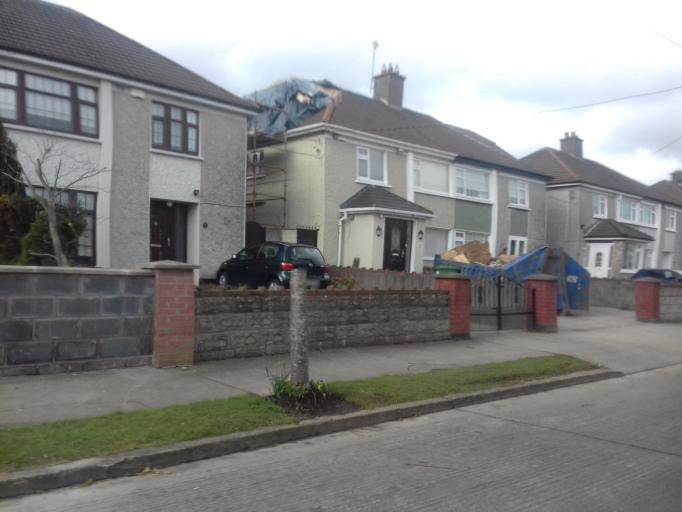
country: IE
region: Leinster
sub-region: Dublin City
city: Finglas
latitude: 53.3947
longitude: -6.2828
